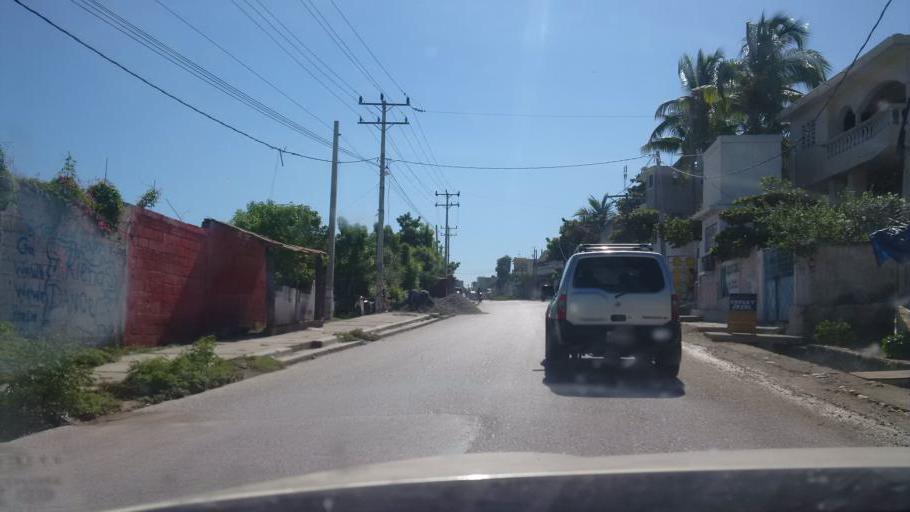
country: HT
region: Artibonite
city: Saint-Marc
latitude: 19.0945
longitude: -72.7134
